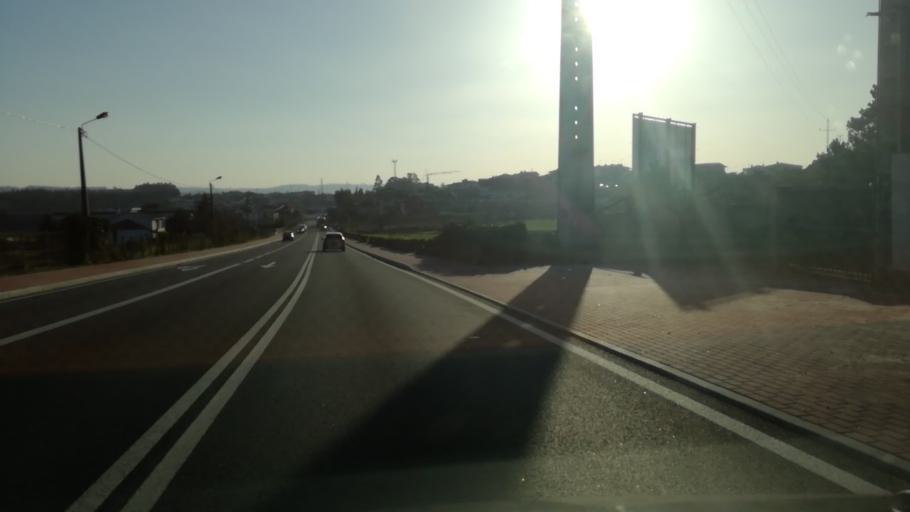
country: PT
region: Braga
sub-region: Vila Nova de Famalicao
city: Ferreiros
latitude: 41.3625
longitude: -8.5474
